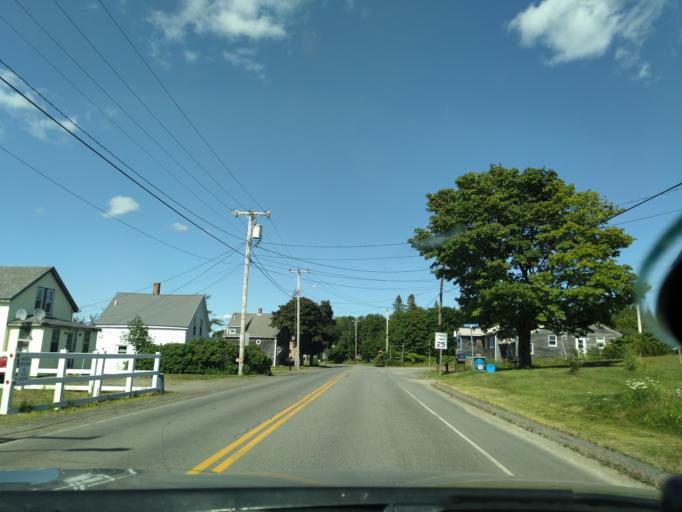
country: US
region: Maine
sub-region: Washington County
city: Eastport
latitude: 44.8523
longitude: -66.9958
